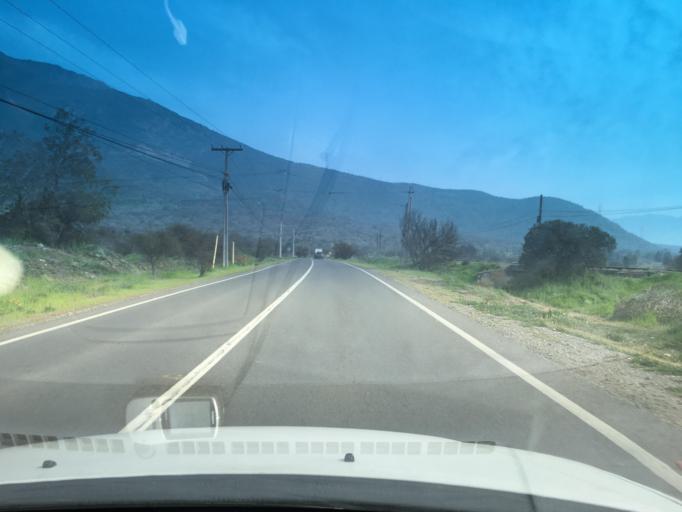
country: CL
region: Santiago Metropolitan
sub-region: Provincia de Chacabuco
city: Lampa
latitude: -33.1514
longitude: -70.9070
